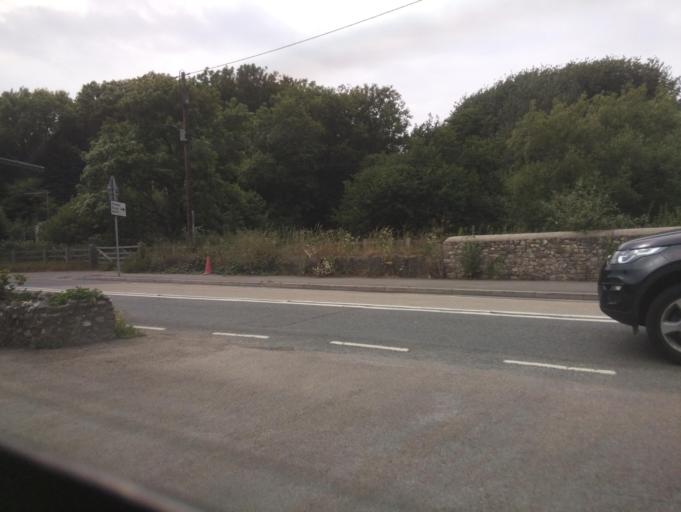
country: GB
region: England
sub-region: Devon
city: Colyton
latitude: 50.7290
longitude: -3.0584
